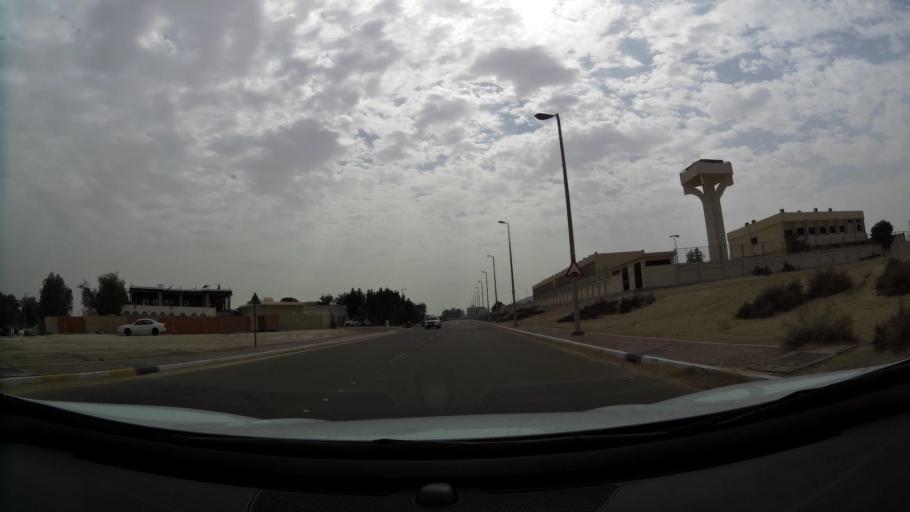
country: AE
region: Abu Dhabi
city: Abu Dhabi
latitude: 24.3168
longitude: 54.6433
